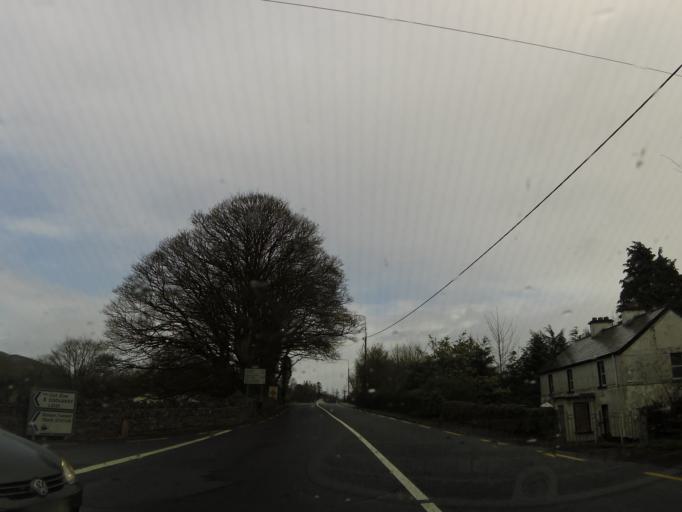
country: IE
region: Connaught
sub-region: Sligo
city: Collooney
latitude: 54.1886
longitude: -8.4925
